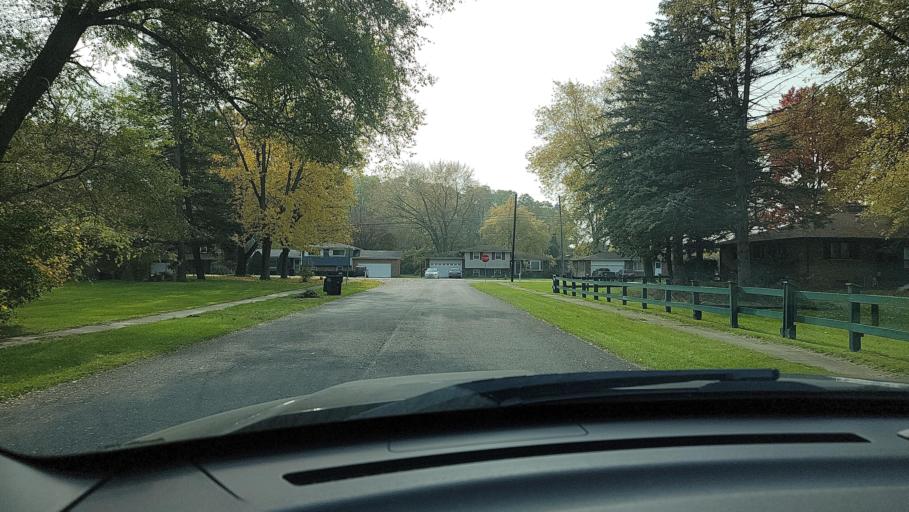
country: US
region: Indiana
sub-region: Porter County
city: Portage
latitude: 41.5948
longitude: -87.1653
